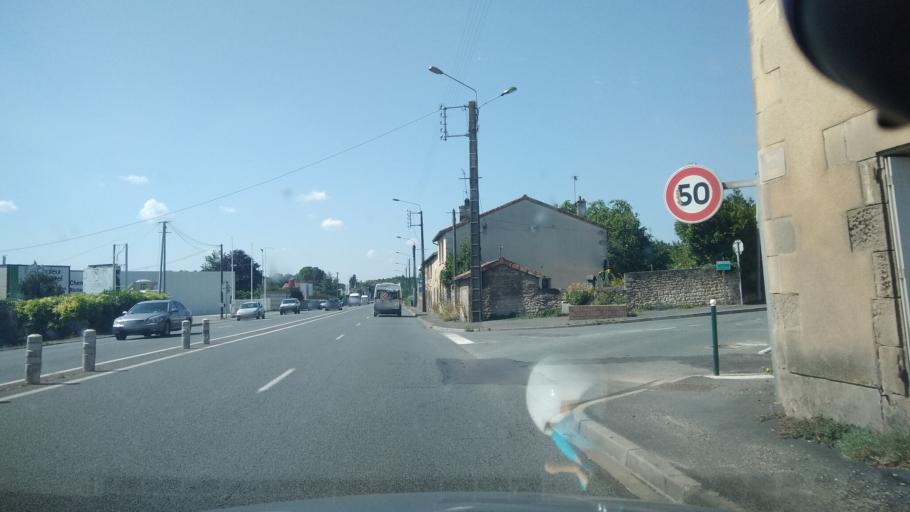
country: FR
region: Poitou-Charentes
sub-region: Departement de la Vienne
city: Chasseneuil-du-Poitou
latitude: 46.6433
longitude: 0.3607
